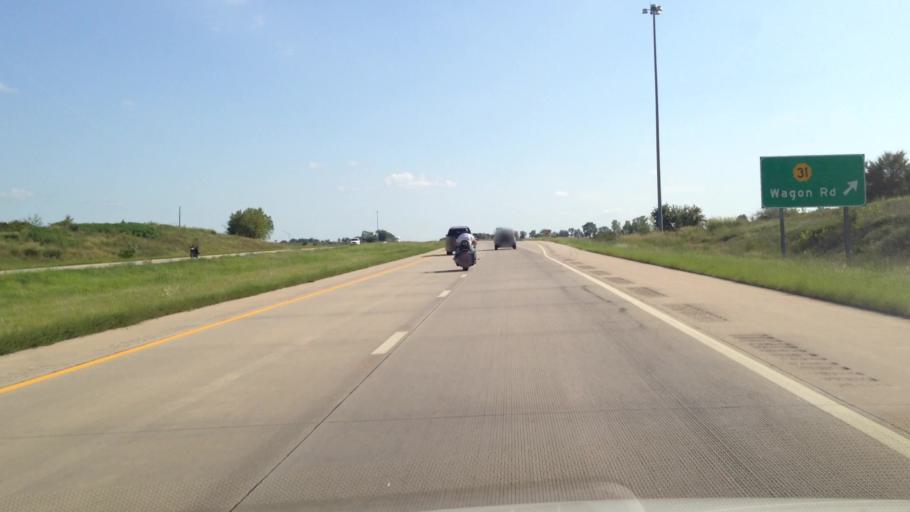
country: US
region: Kansas
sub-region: Bourbon County
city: Fort Scott
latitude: 37.9986
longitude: -94.7051
